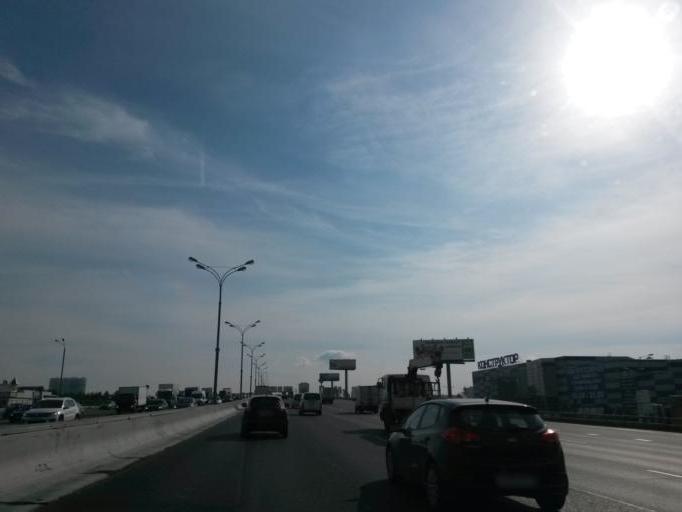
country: RU
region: Moscow
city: Biryulevo
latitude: 55.5833
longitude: 37.7081
